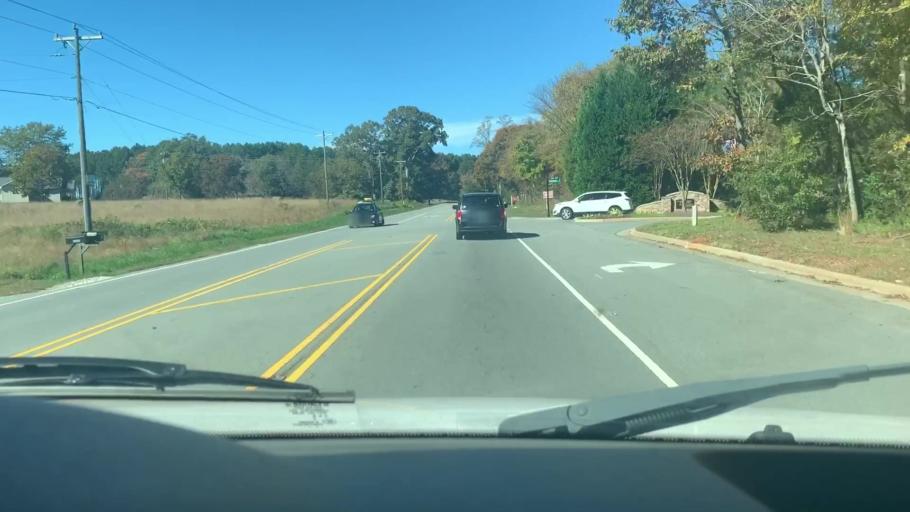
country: US
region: North Carolina
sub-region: Lincoln County
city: Lowesville
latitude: 35.4377
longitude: -80.9769
